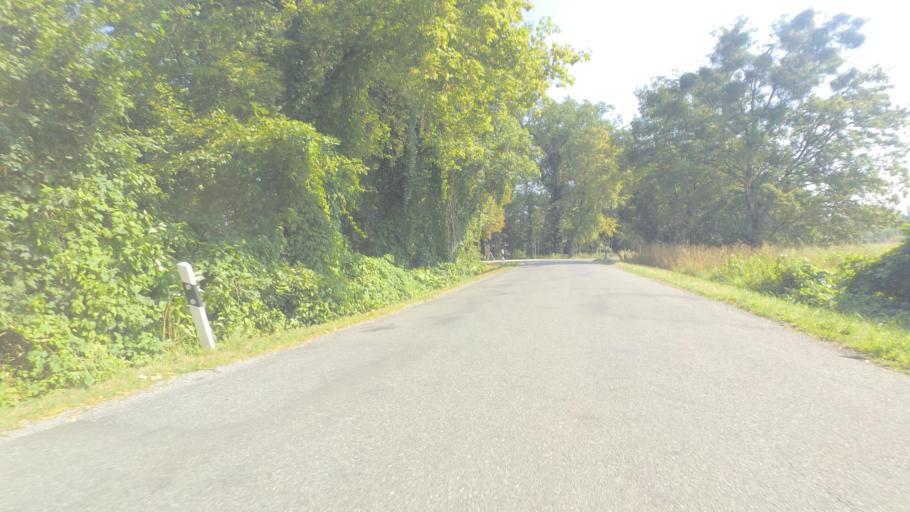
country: DE
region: Mecklenburg-Vorpommern
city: Pampow
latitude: 53.6792
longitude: 12.5611
